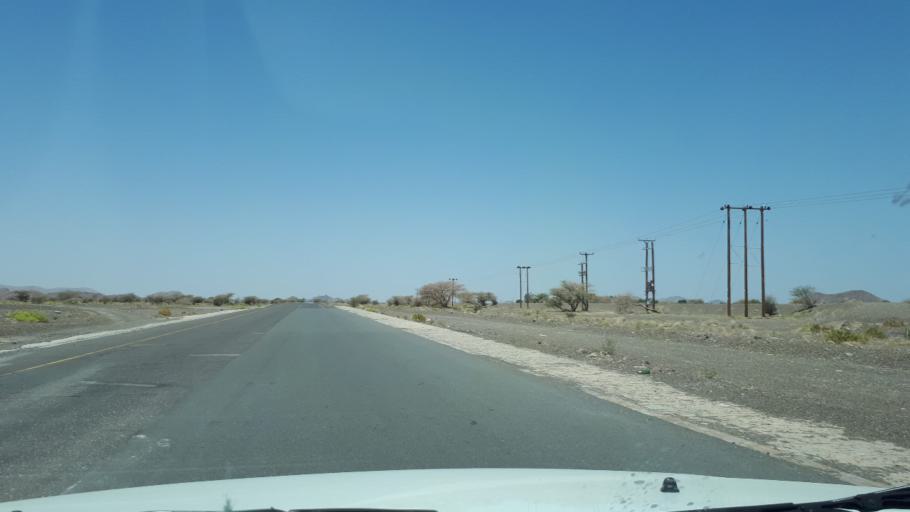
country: OM
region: Ash Sharqiyah
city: Ibra'
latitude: 22.6171
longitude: 58.4281
